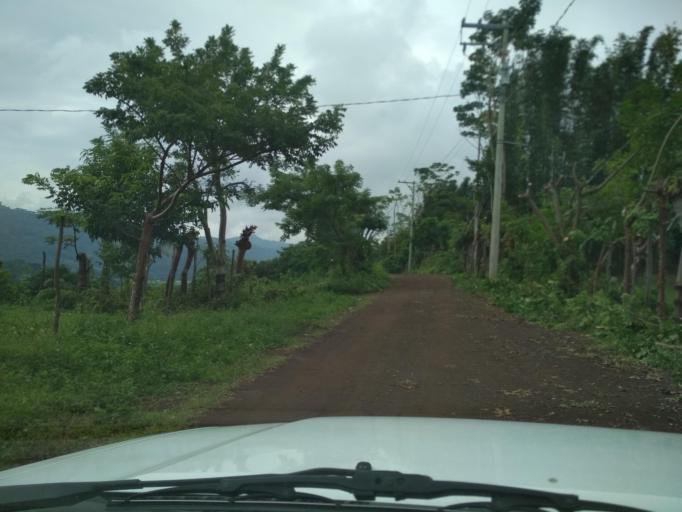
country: MX
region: Veracruz
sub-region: San Andres Tuxtla
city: Matacapan
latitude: 18.4387
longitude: -95.1497
